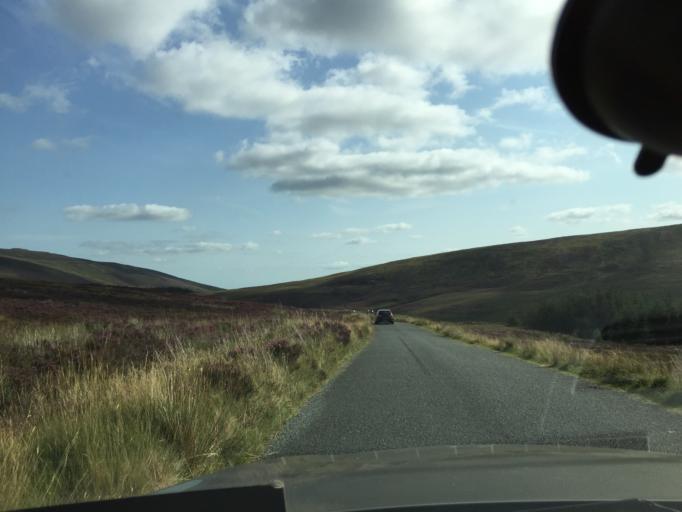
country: IE
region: Leinster
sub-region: Wicklow
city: Rathdrum
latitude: 53.0747
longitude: -6.3531
